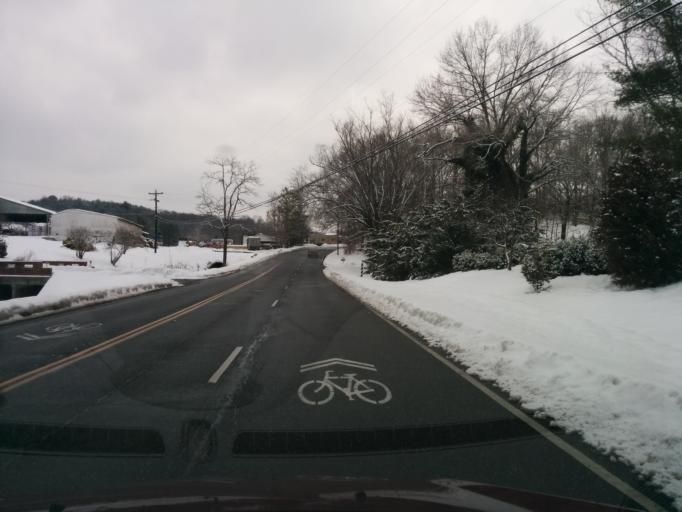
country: US
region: Virginia
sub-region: City of Lexington
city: Lexington
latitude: 37.7731
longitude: -79.4496
